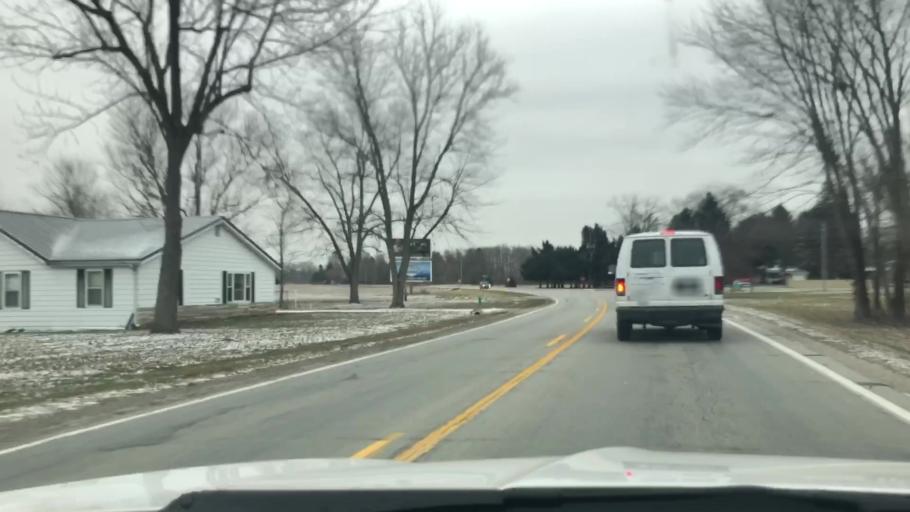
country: US
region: Indiana
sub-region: Fulton County
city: Rochester
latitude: 41.0586
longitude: -86.1696
